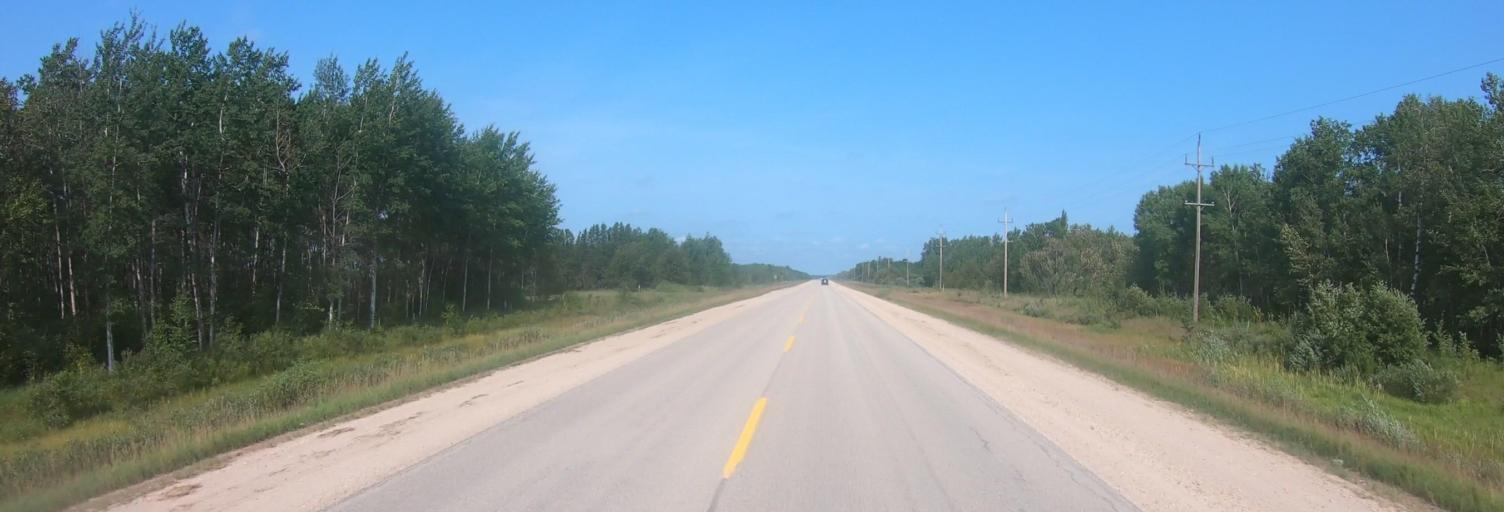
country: US
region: Minnesota
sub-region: Roseau County
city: Roseau
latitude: 49.1422
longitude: -96.1078
